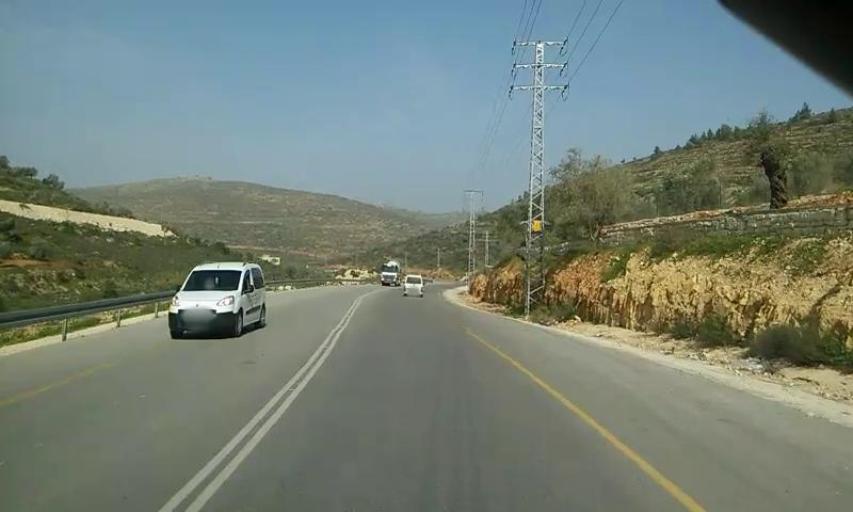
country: PS
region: West Bank
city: Dura al Qar`
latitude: 31.9825
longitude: 35.2342
